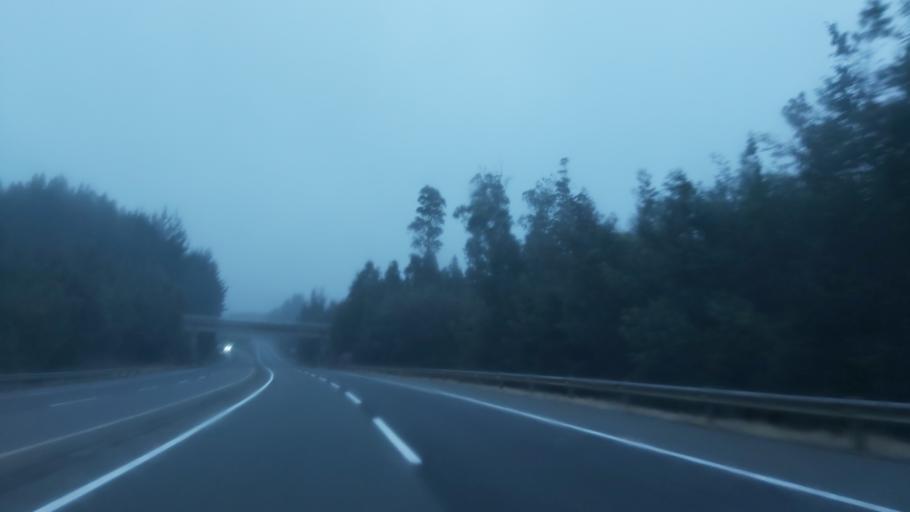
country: CL
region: Biobio
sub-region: Provincia de Concepcion
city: Penco
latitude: -36.7428
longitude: -72.9116
